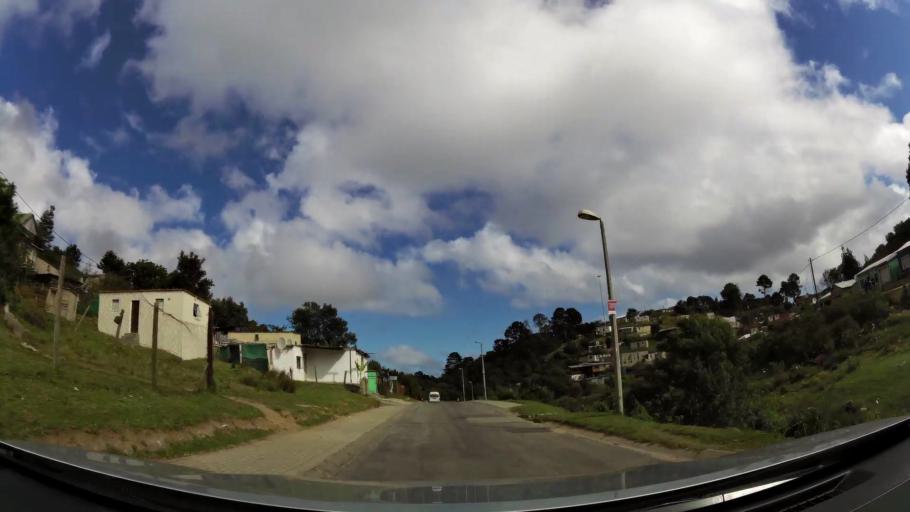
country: ZA
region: Western Cape
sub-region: Eden District Municipality
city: Knysna
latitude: -34.0339
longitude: 23.1025
